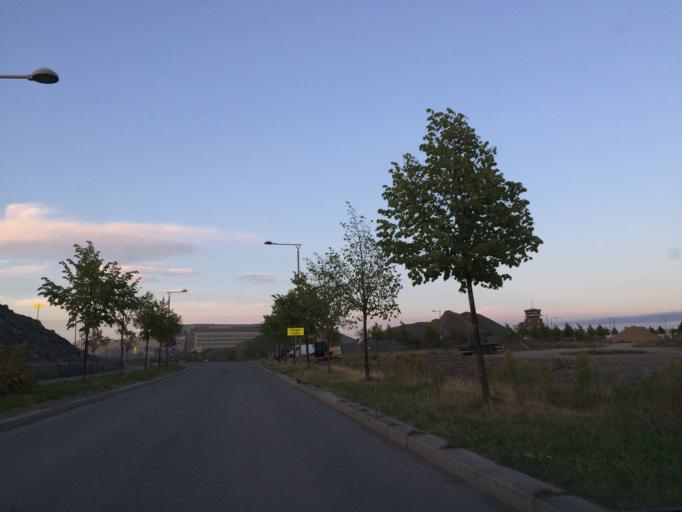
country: NO
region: Akershus
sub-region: Baerum
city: Lysaker
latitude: 59.9003
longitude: 10.6150
